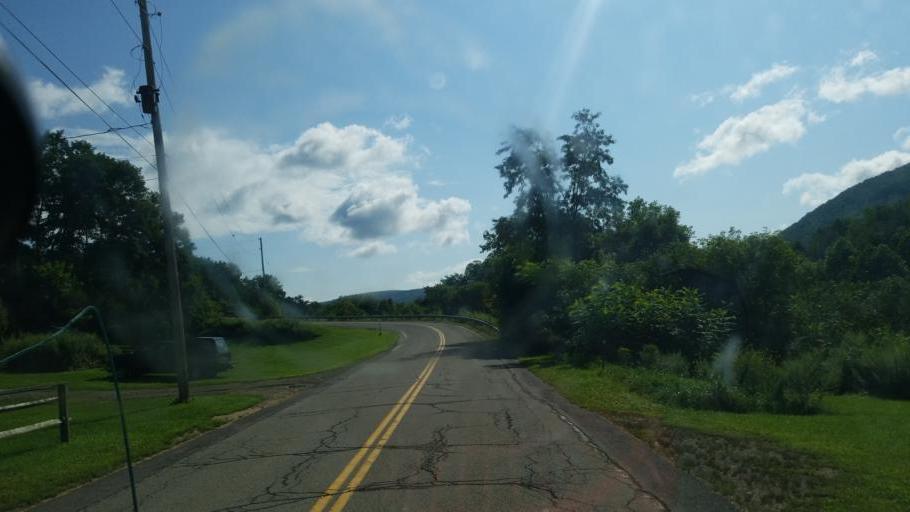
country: US
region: New York
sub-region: Steuben County
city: Canisteo
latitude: 42.2645
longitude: -77.5785
